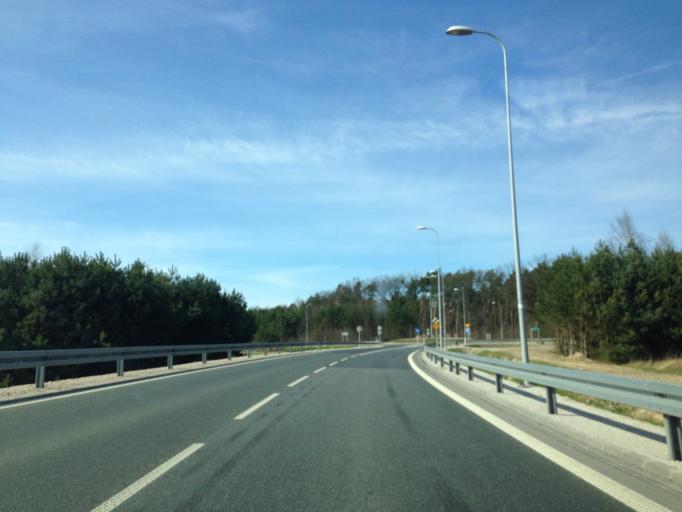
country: PL
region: Lodz Voivodeship
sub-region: Powiat sieradzki
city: Sieradz
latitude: 51.6015
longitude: 18.8129
